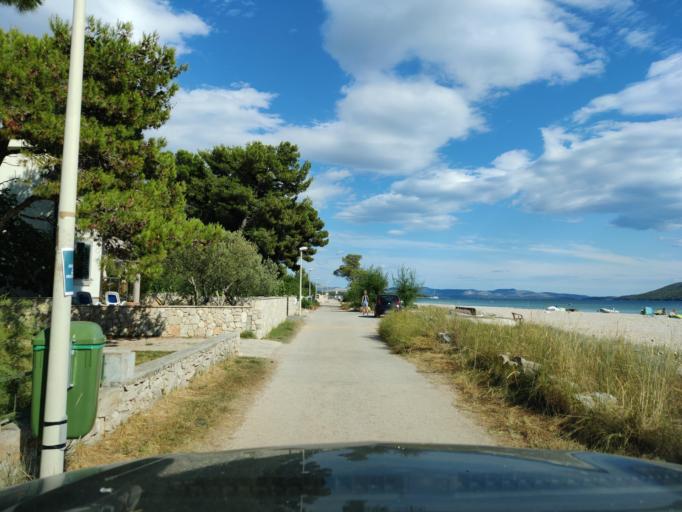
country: HR
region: Sibensko-Kniniska
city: Zaton
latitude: 43.7268
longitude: 15.8394
